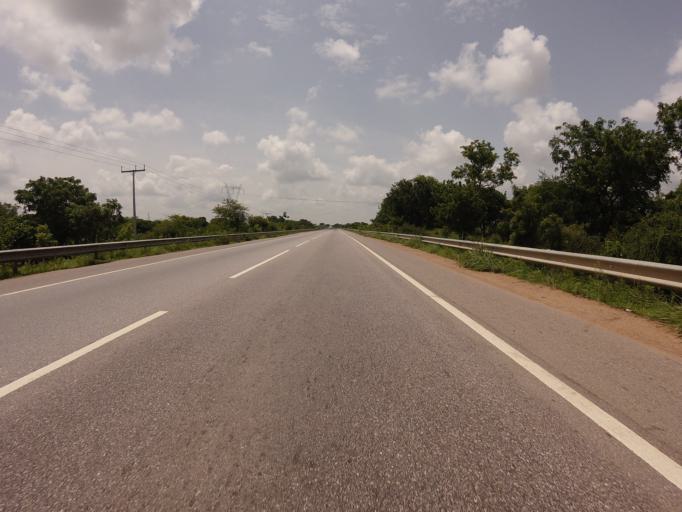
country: GH
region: Northern
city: Tamale
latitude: 9.1409
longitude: -1.1726
